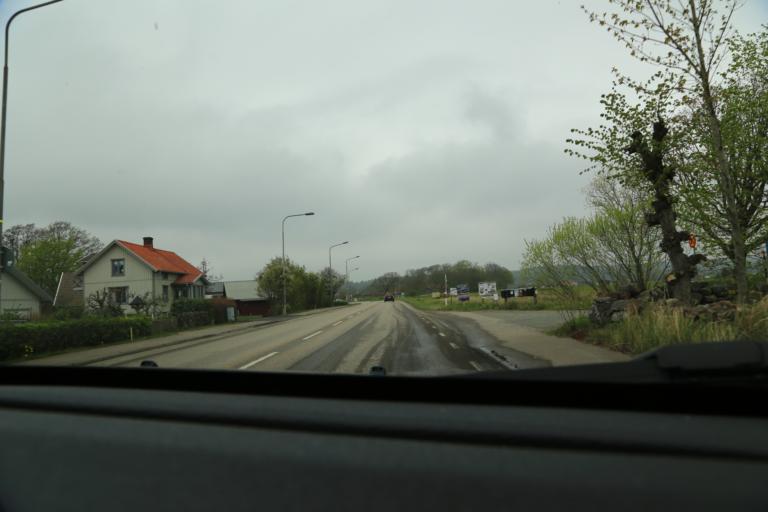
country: SE
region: Halland
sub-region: Varbergs Kommun
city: Veddige
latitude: 57.2208
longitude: 12.2218
